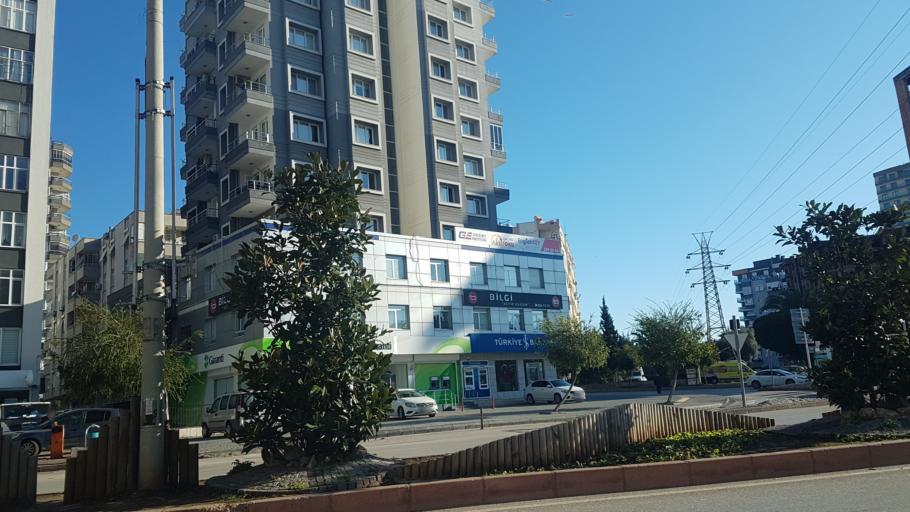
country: TR
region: Adana
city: Adana
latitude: 37.0161
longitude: 35.3214
